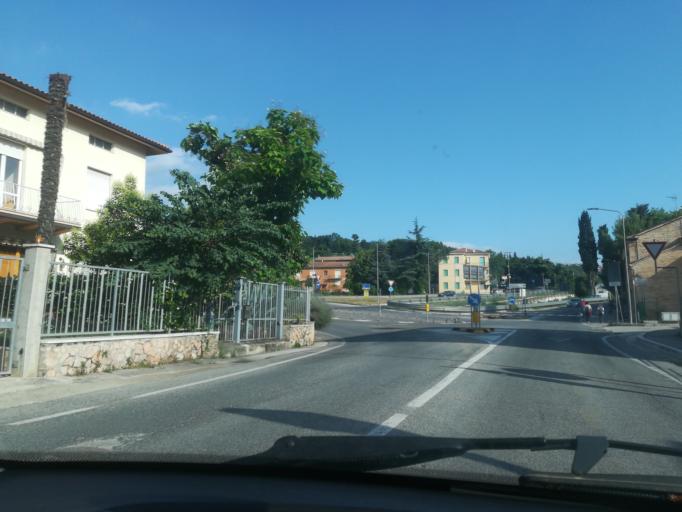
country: IT
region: The Marches
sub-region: Provincia di Macerata
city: Villa Potenza
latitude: 43.3208
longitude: 13.4271
